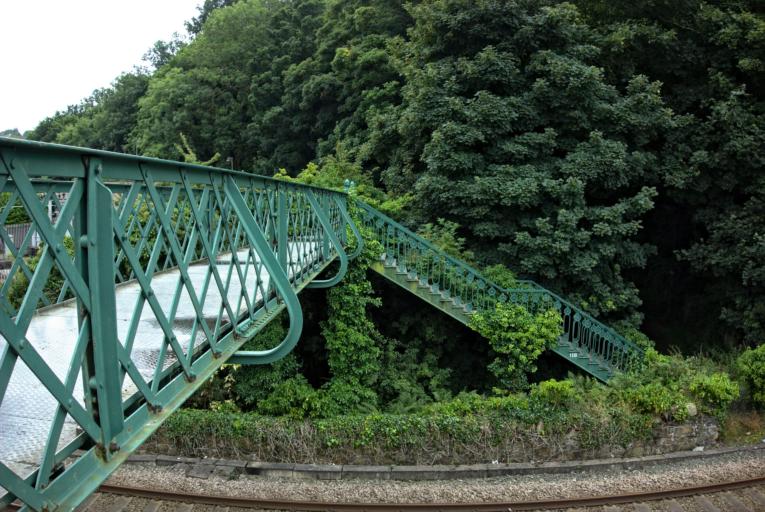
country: GB
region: Wales
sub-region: Conwy
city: Conwy
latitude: 53.2844
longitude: -3.8383
